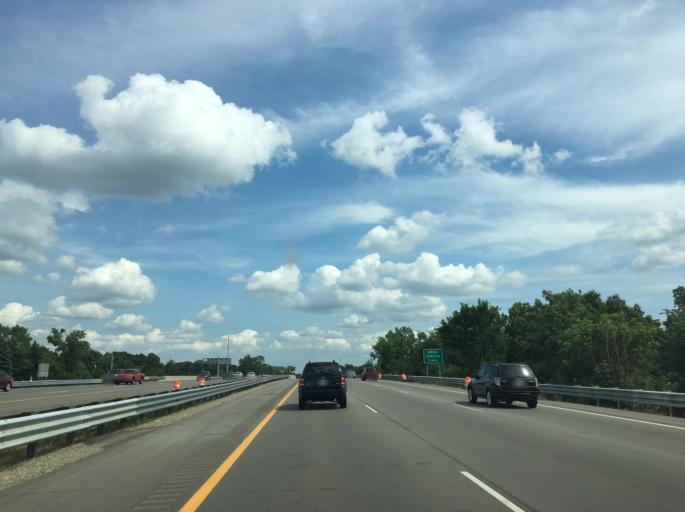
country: US
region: Michigan
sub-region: Oakland County
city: Waterford
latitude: 42.7221
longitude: -83.3510
